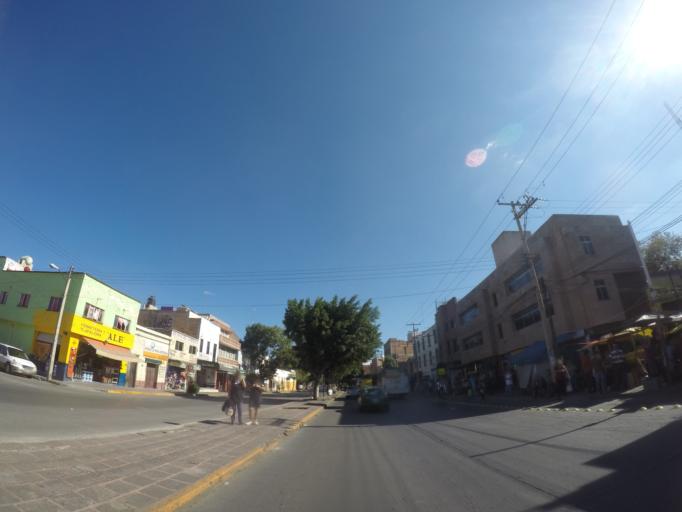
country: MX
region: San Luis Potosi
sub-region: San Luis Potosi
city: San Luis Potosi
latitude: 22.1576
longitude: -100.9746
